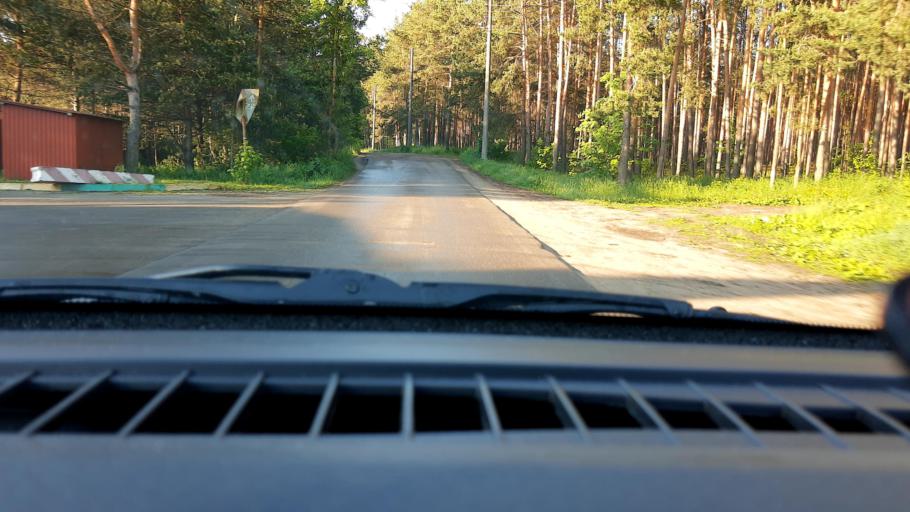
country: RU
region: Nizjnij Novgorod
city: Gorbatovka
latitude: 56.3079
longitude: 43.7395
